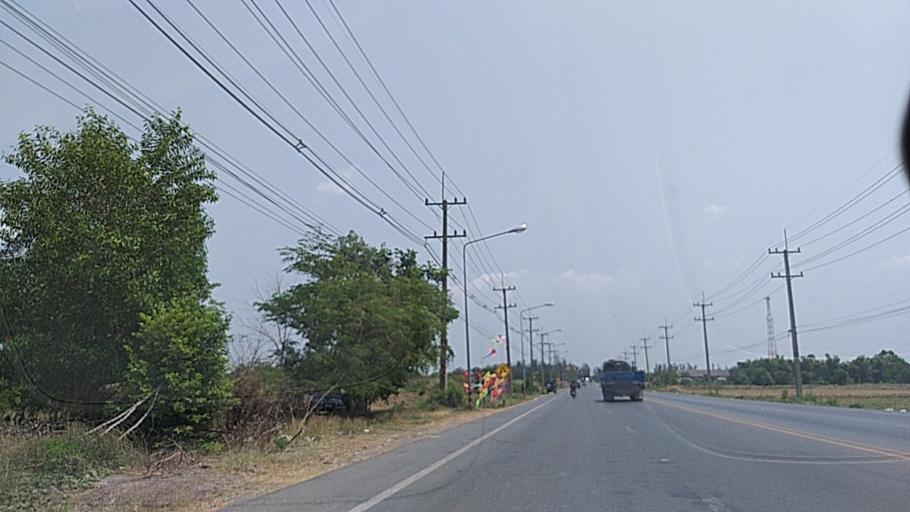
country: TH
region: Bangkok
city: Nong Chok
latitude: 13.9695
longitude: 100.9547
